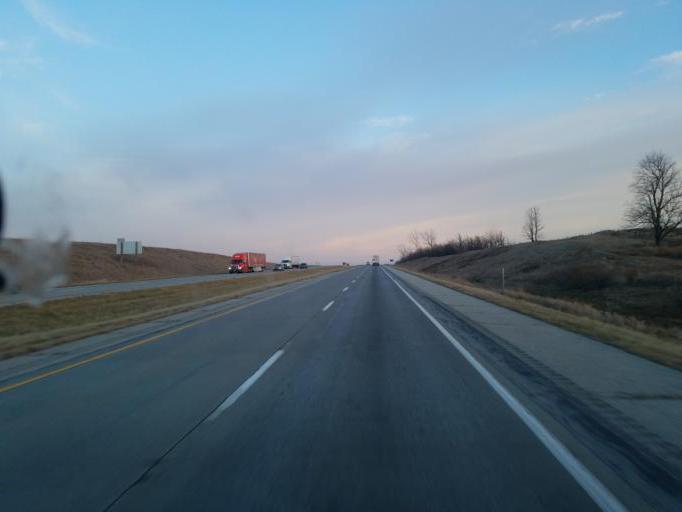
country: US
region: Iowa
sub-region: Pottawattamie County
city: Avoca
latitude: 41.4999
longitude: -95.5145
